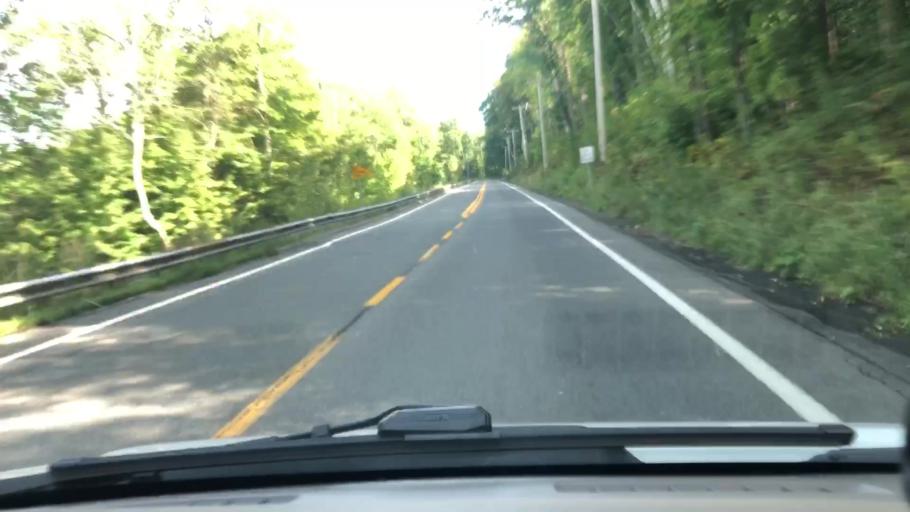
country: US
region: Massachusetts
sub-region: Berkshire County
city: North Adams
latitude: 42.7022
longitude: -73.0694
